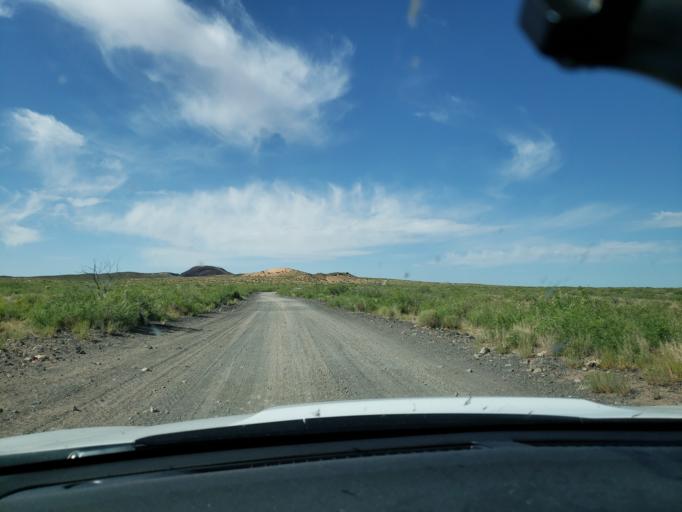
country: US
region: New Mexico
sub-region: Dona Ana County
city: San Miguel
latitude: 32.0861
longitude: -106.7880
